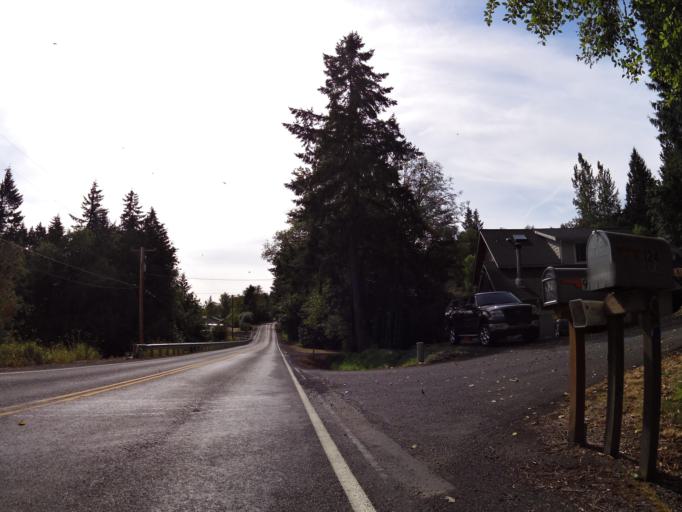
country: US
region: Washington
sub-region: Lewis County
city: Chehalis
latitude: 46.6315
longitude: -122.9692
